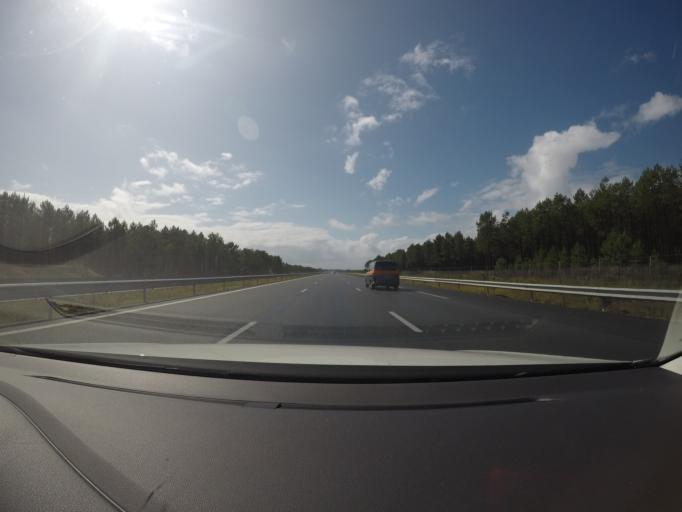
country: FR
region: Aquitaine
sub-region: Departement des Landes
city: Castets
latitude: 43.9162
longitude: -1.1182
